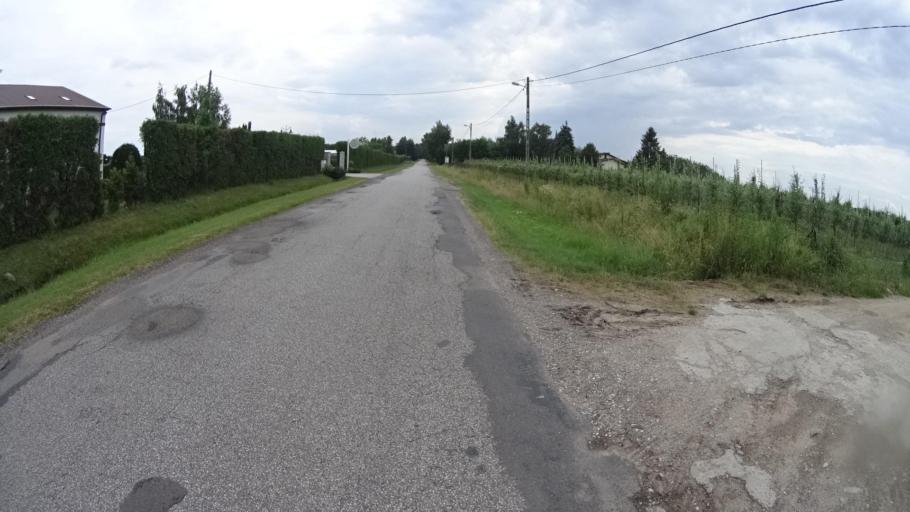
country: PL
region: Masovian Voivodeship
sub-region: Powiat grojecki
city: Goszczyn
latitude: 51.7889
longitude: 20.8561
